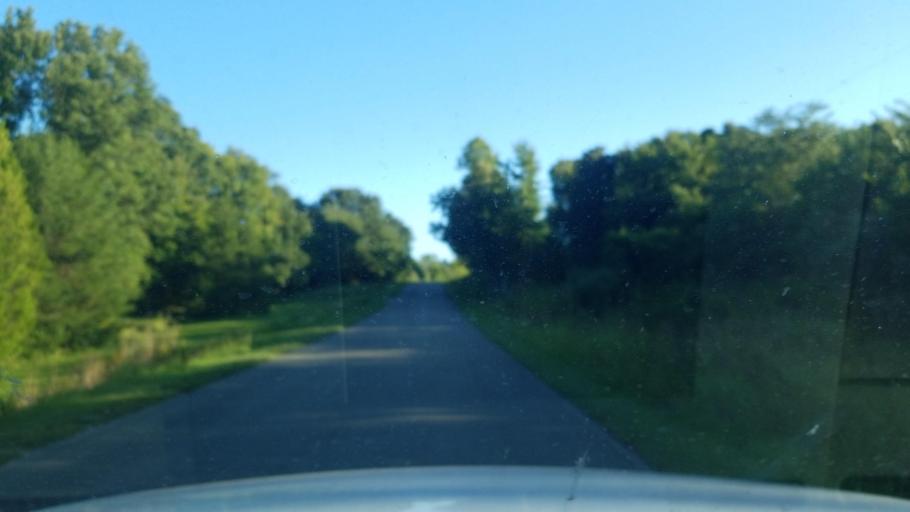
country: US
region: Illinois
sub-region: Hardin County
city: Elizabethtown
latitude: 37.5896
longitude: -88.3656
